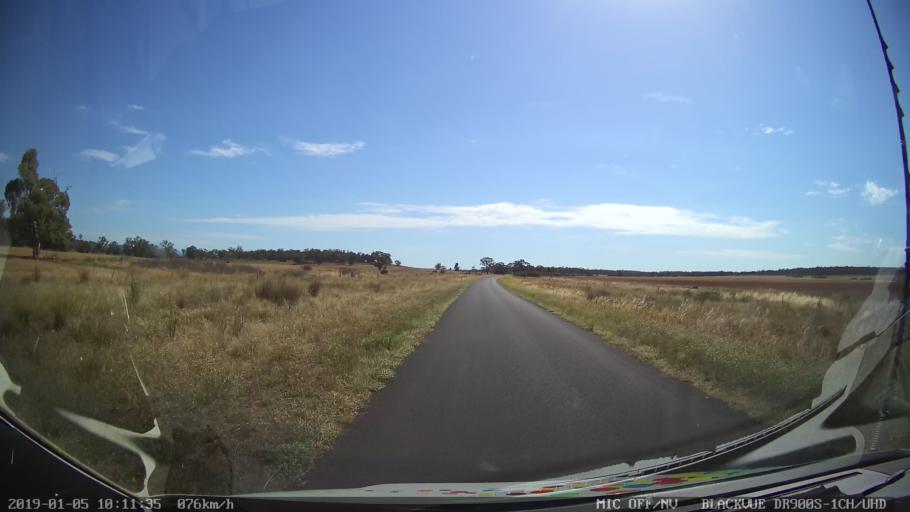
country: AU
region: New South Wales
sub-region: Gilgandra
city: Gilgandra
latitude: -31.6125
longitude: 148.9028
